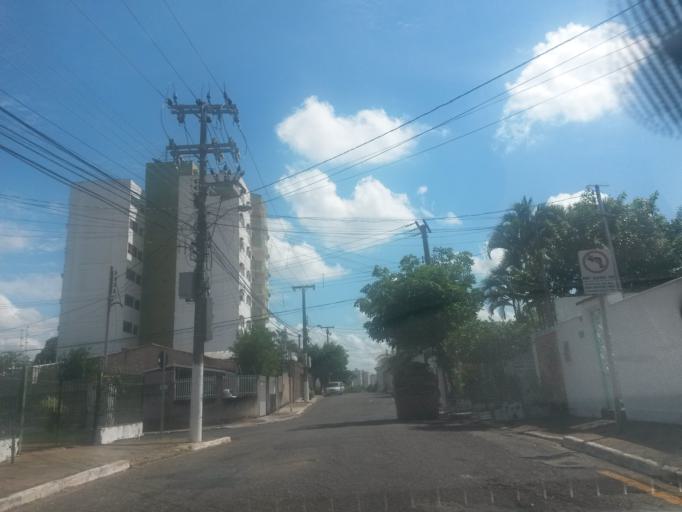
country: BR
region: Mato Grosso
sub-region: Cuiaba
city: Cuiaba
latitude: -15.5957
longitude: -56.0866
